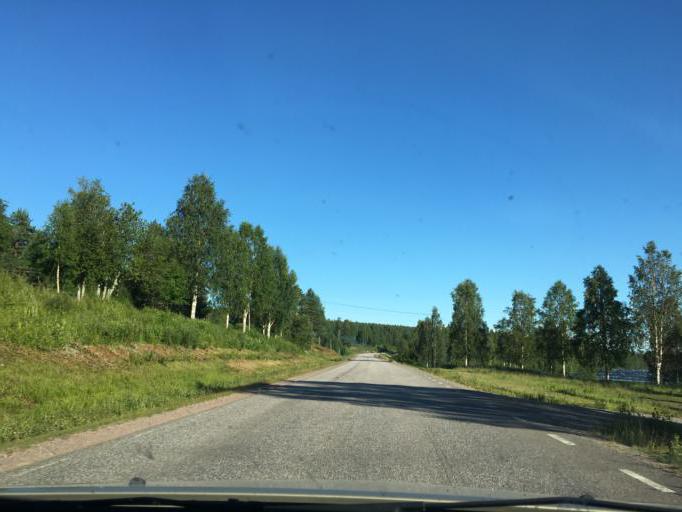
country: SE
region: Norrbotten
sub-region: Kalix Kommun
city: Rolfs
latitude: 65.9176
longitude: 22.9183
